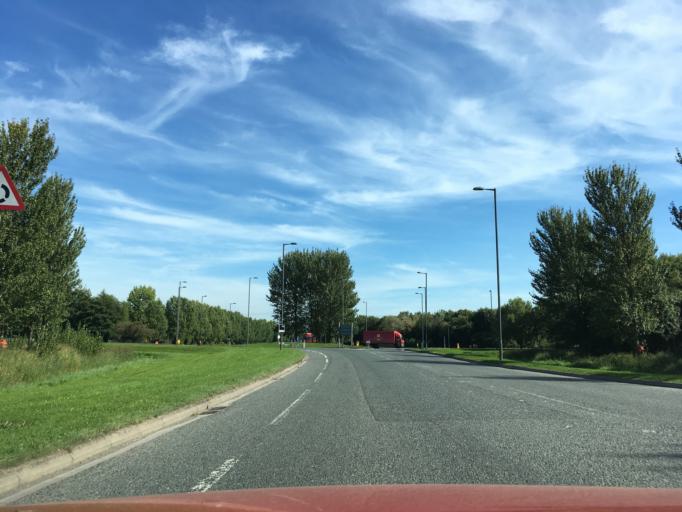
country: GB
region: England
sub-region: South Gloucestershire
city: Severn Beach
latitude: 51.5520
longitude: -2.6525
